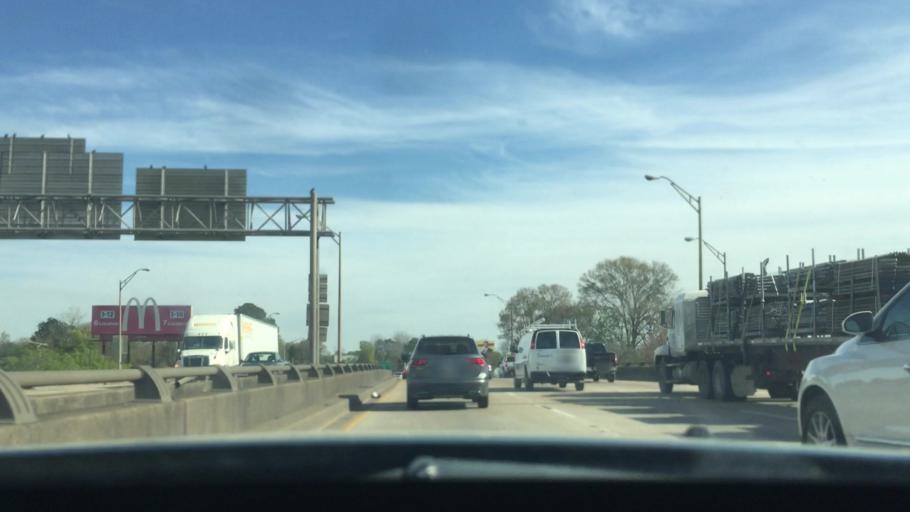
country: US
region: Louisiana
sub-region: East Baton Rouge Parish
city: Baton Rouge
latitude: 30.4316
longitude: -91.1749
